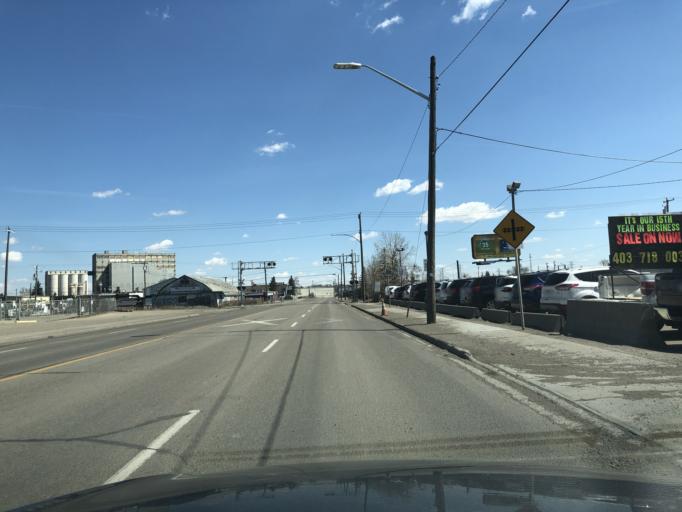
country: CA
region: Alberta
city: Calgary
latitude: 51.0186
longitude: -114.0265
